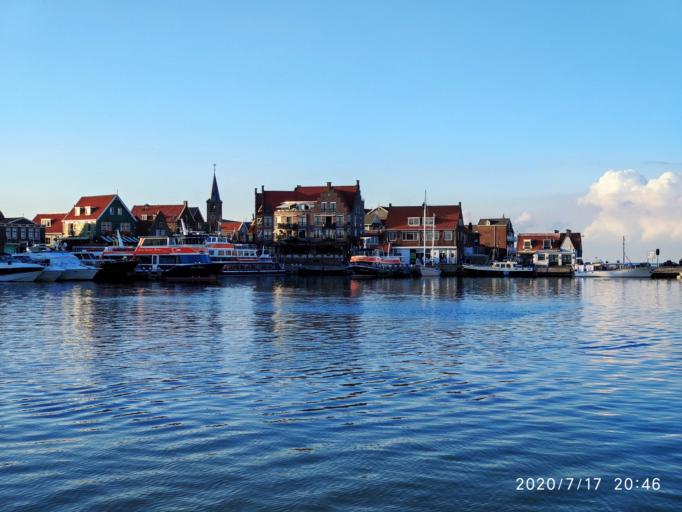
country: NL
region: North Holland
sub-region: Gemeente Edam-Volendam
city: Volendam
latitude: 52.4926
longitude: 5.0762
